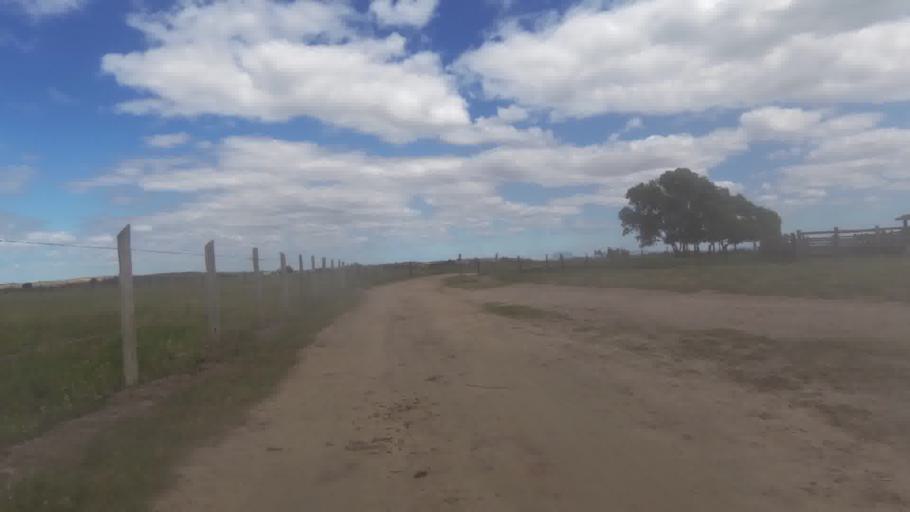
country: BR
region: Espirito Santo
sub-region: Marataizes
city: Marataizes
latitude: -21.2383
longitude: -40.9978
